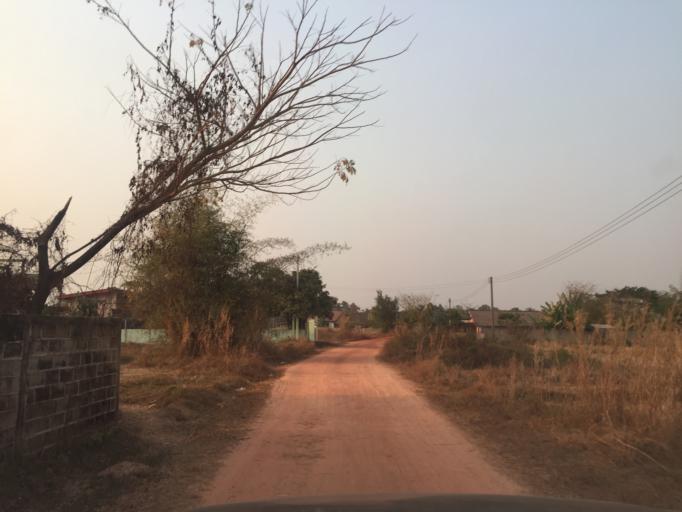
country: LA
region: Vientiane
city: Vientiane
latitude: 18.0585
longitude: 102.5210
